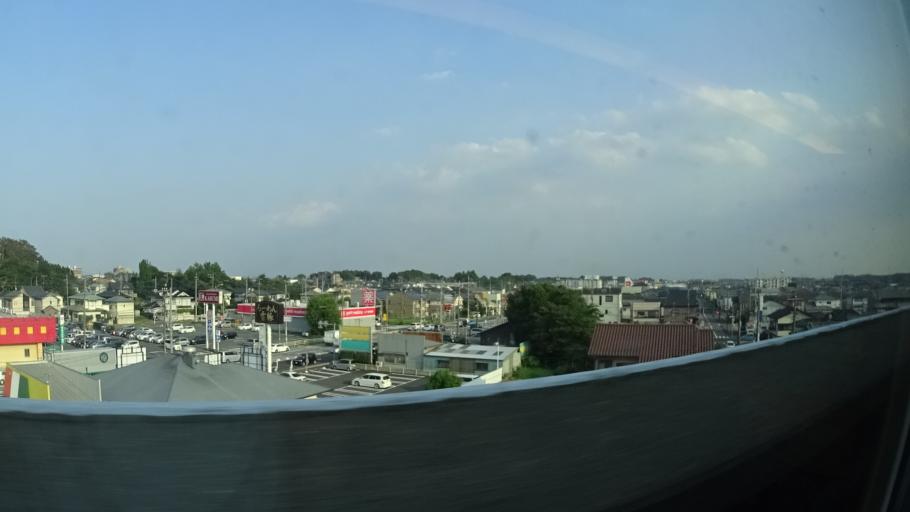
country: JP
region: Saitama
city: Shiraoka
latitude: 36.0182
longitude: 139.6532
